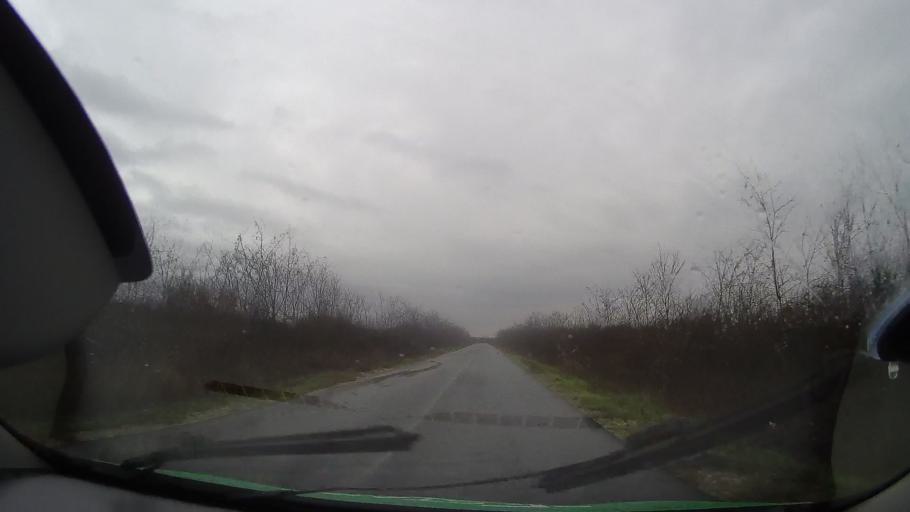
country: RO
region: Bihor
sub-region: Comuna Cociuba Mare
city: Cociuba Mare
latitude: 46.6983
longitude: 22.0326
